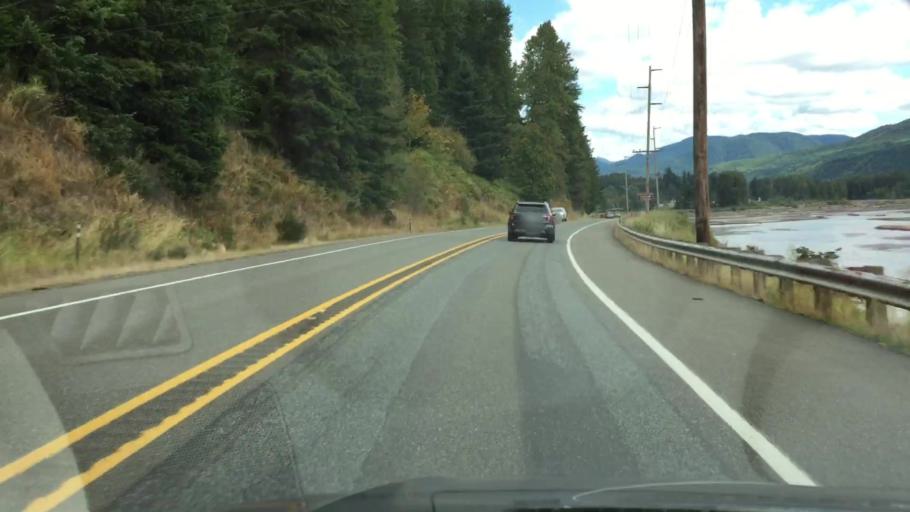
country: US
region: Washington
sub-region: Pierce County
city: Eatonville
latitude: 46.7710
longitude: -122.2099
